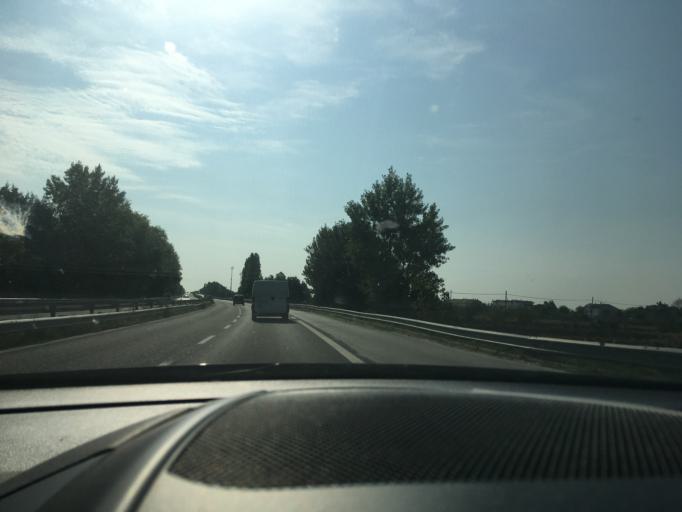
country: IT
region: Emilia-Romagna
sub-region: Forli-Cesena
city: San Mauro a Mare
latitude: 44.1496
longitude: 12.4445
